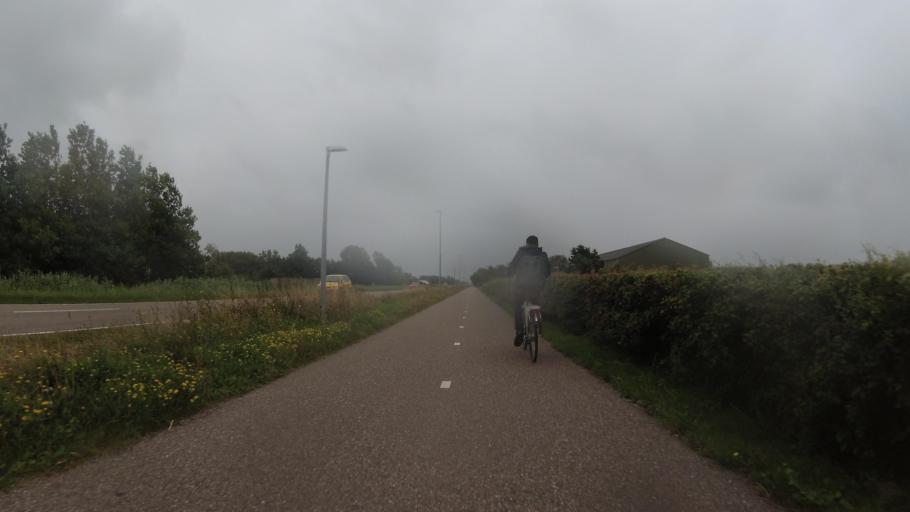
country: NL
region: North Holland
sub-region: Gemeente Den Helder
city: Den Helder
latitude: 52.9119
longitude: 4.7535
